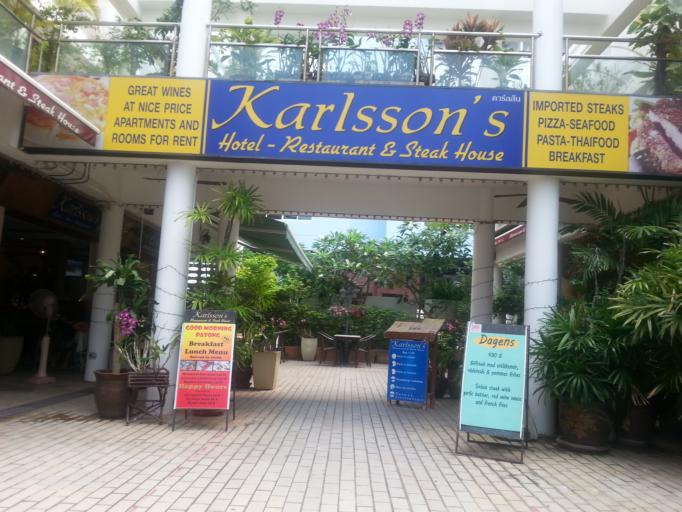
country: TH
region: Phuket
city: Patong
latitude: 7.8919
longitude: 98.2952
